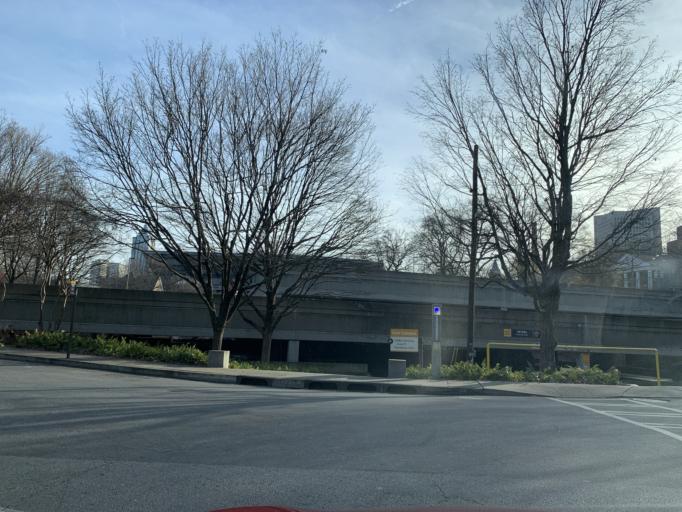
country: US
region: Georgia
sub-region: Fulton County
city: Atlanta
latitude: 33.7761
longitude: -84.3937
